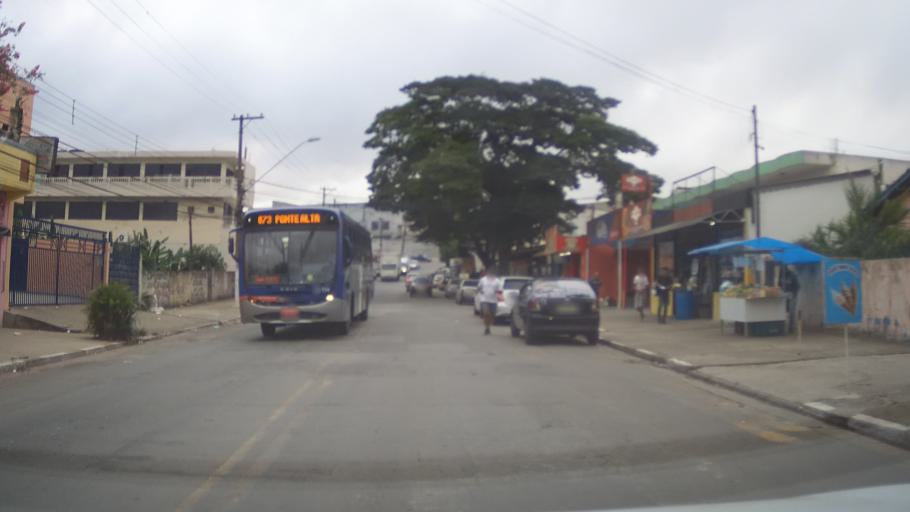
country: BR
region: Sao Paulo
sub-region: Aruja
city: Aruja
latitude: -23.4075
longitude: -46.3921
